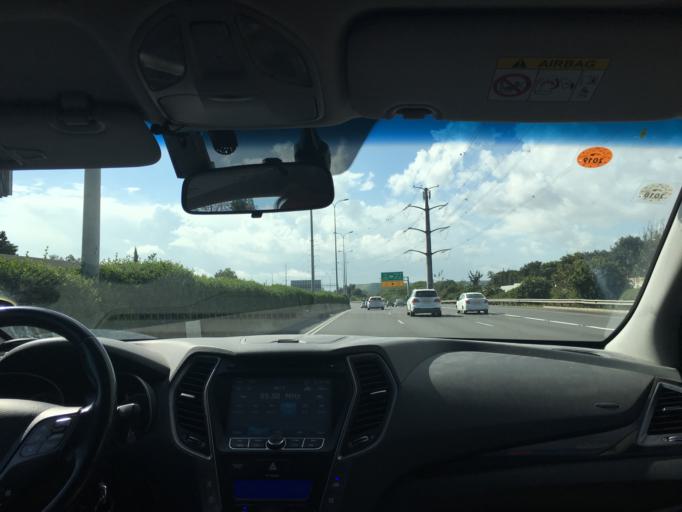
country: IL
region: Tel Aviv
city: Giv`atayim
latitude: 32.0490
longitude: 34.8309
